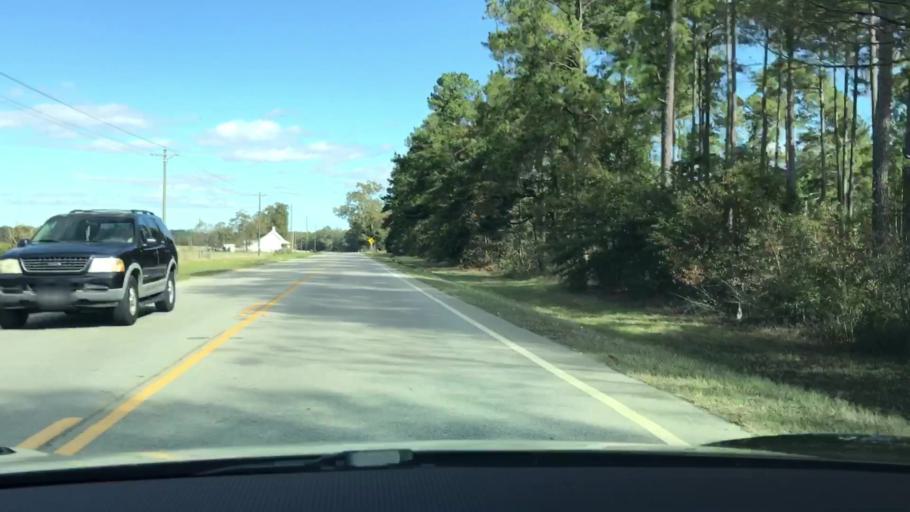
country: US
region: Georgia
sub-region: Jefferson County
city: Wrens
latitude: 33.1745
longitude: -82.4538
